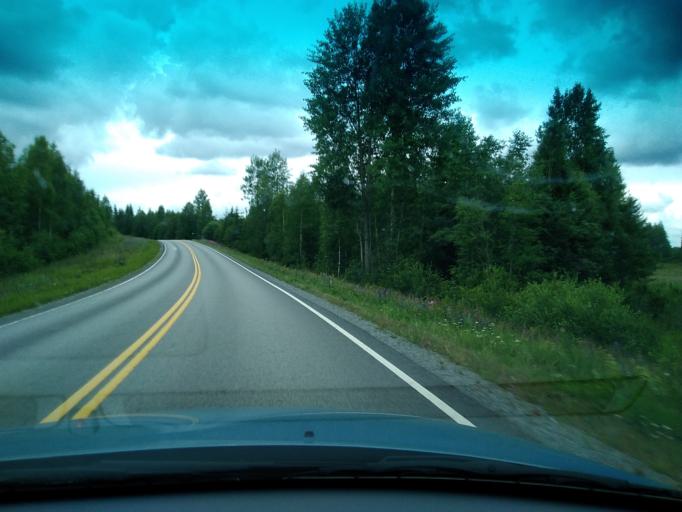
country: FI
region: Central Finland
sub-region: Saarijaervi-Viitasaari
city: Pylkoenmaeki
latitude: 62.6500
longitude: 24.9924
